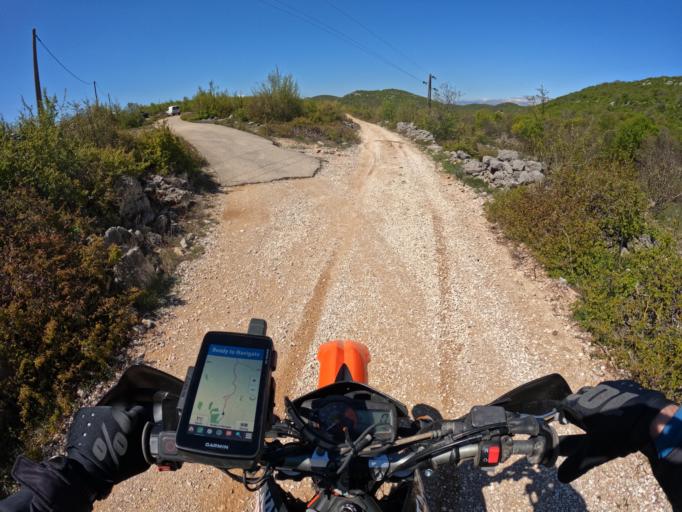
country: HR
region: Zadarska
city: Obrovac
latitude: 44.1257
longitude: 15.7912
